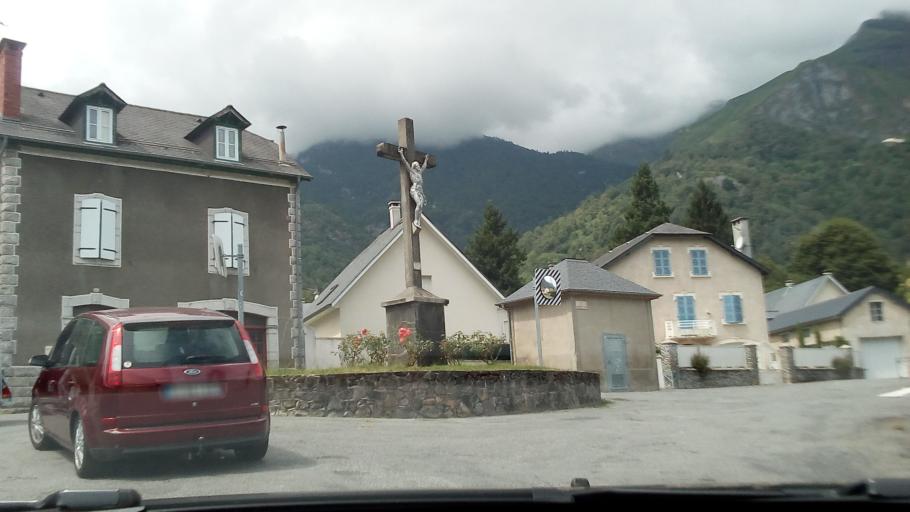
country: FR
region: Aquitaine
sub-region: Departement des Pyrenees-Atlantiques
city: Laruns
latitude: 42.9859
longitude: -0.4235
